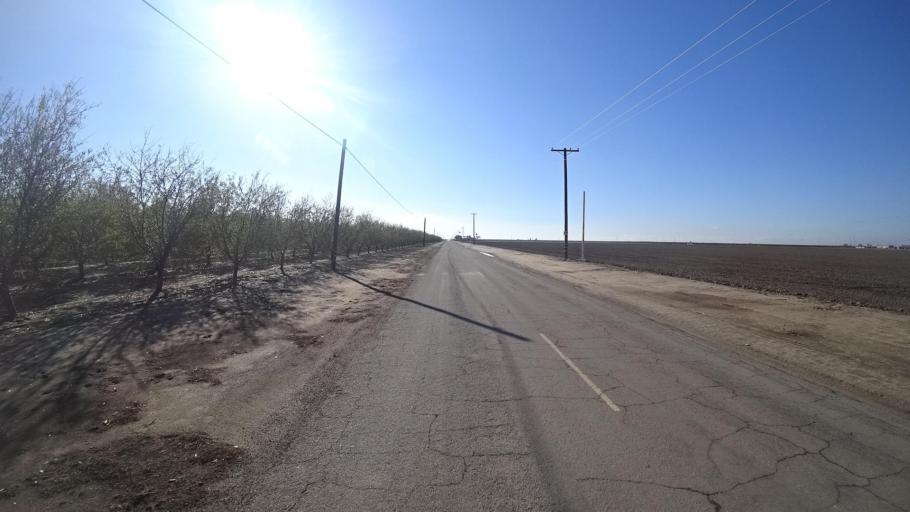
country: US
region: California
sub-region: Kern County
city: McFarland
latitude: 35.7084
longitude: -119.2763
